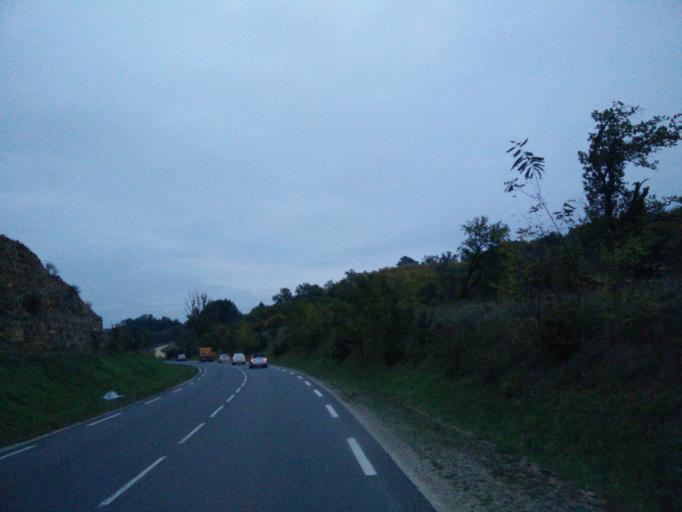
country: FR
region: Aquitaine
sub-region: Departement de la Dordogne
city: Sarlat-la-Caneda
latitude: 44.8845
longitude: 1.2027
